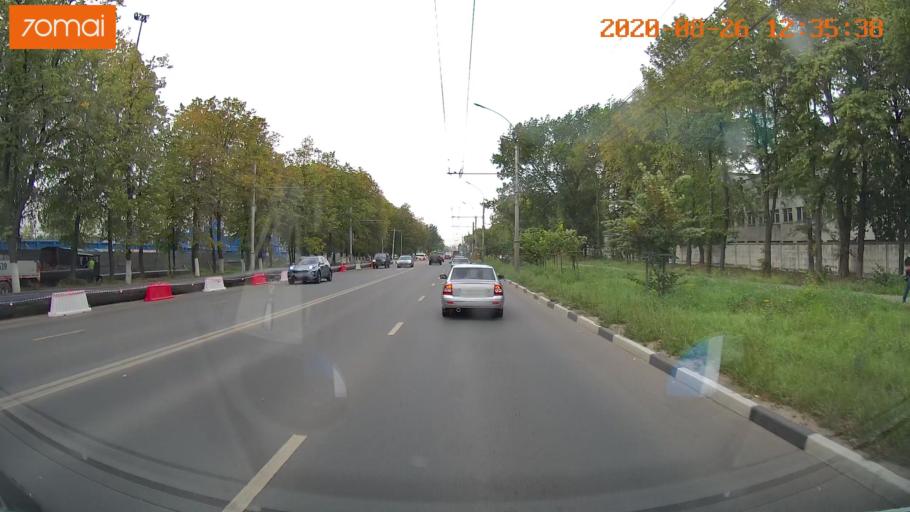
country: RU
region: Rjazan
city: Ryazan'
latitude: 54.5973
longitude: 39.7675
